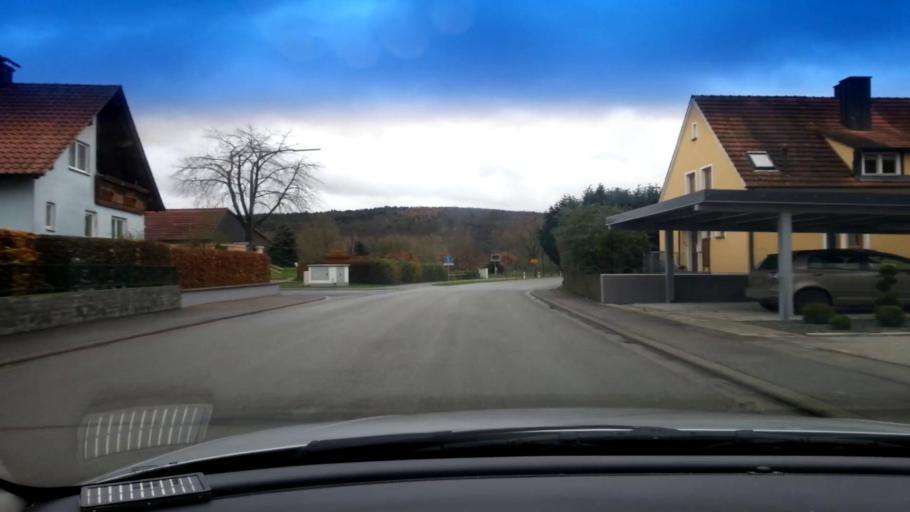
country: DE
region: Bavaria
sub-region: Upper Franconia
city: Rattelsdorf
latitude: 50.0066
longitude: 10.9076
